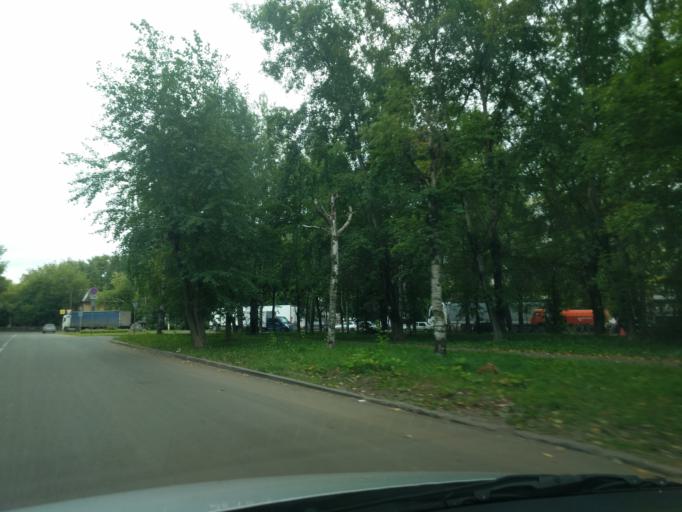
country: RU
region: Kirov
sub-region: Kirovo-Chepetskiy Rayon
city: Kirov
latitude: 58.6339
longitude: 49.6181
